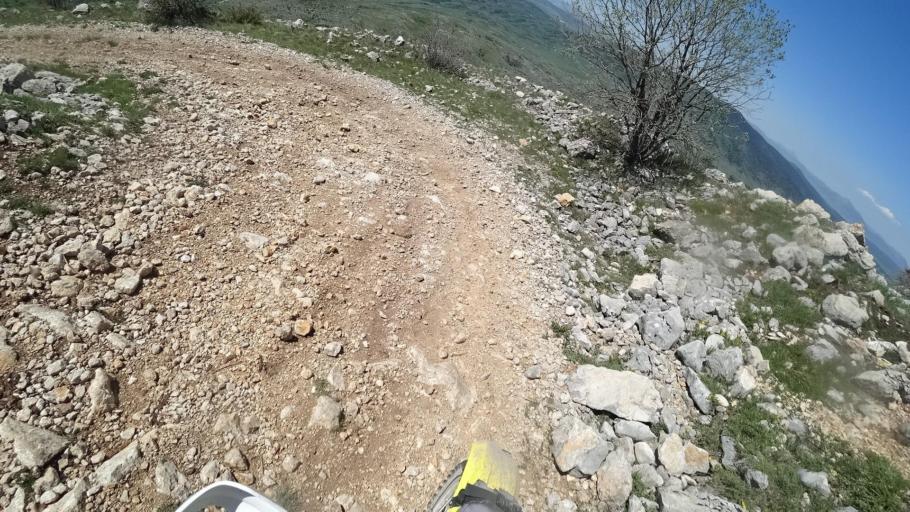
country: BA
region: Federation of Bosnia and Herzegovina
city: Rumboci
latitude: 43.8431
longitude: 17.4491
